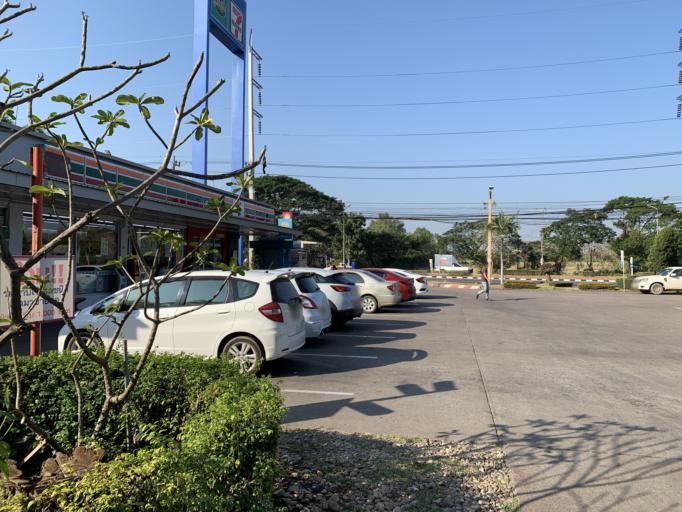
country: TH
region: Uttaradit
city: Uttaradit
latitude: 17.6050
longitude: 100.1241
